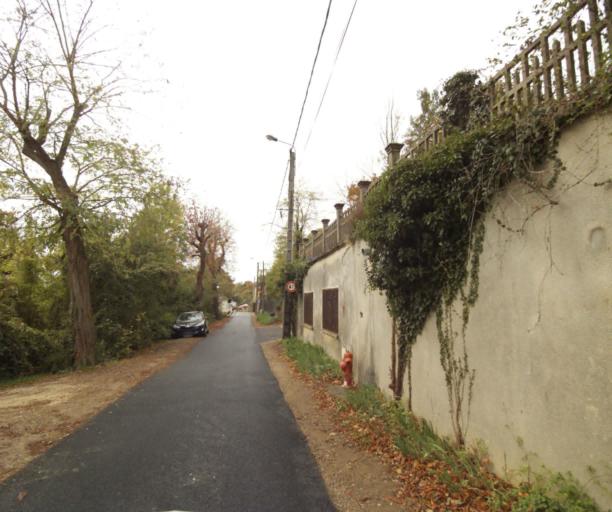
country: FR
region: Centre
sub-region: Departement d'Eure-et-Loir
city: Dreux
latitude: 48.7406
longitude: 1.3683
